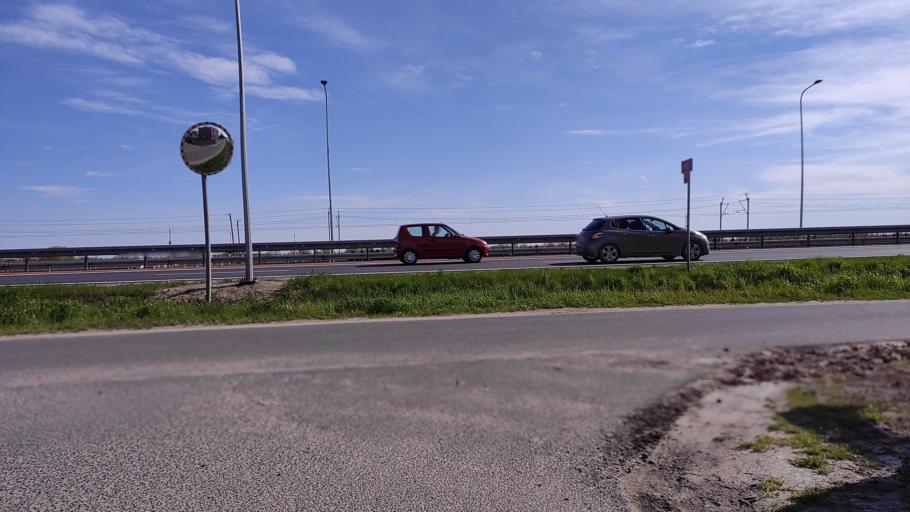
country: PL
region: Greater Poland Voivodeship
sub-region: Powiat poznanski
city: Kostrzyn
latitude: 52.3963
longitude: 17.1780
